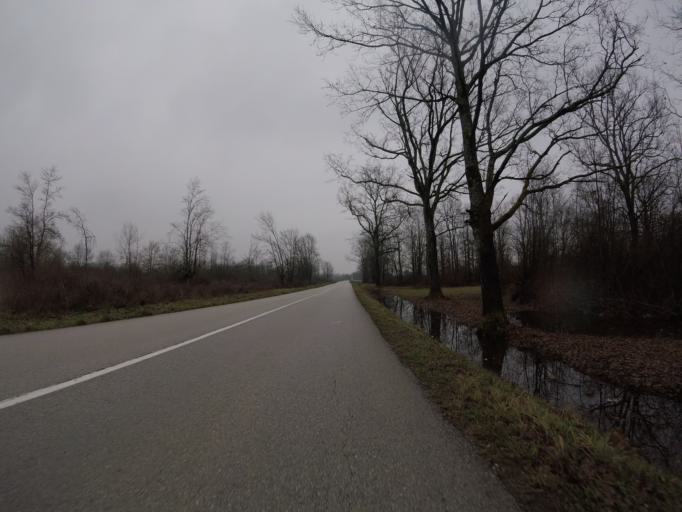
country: HR
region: Zagrebacka
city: Kuce
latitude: 45.7046
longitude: 16.1967
